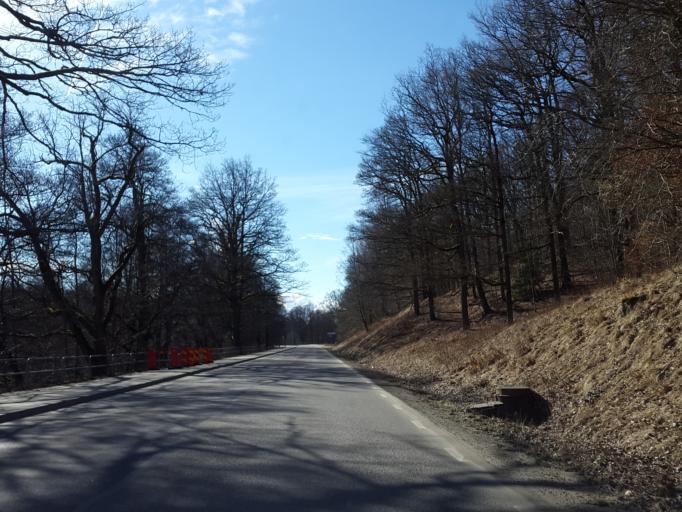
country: SE
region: Vaestra Goetaland
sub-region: Boras Kommun
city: Boras
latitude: 57.7376
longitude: 12.9286
